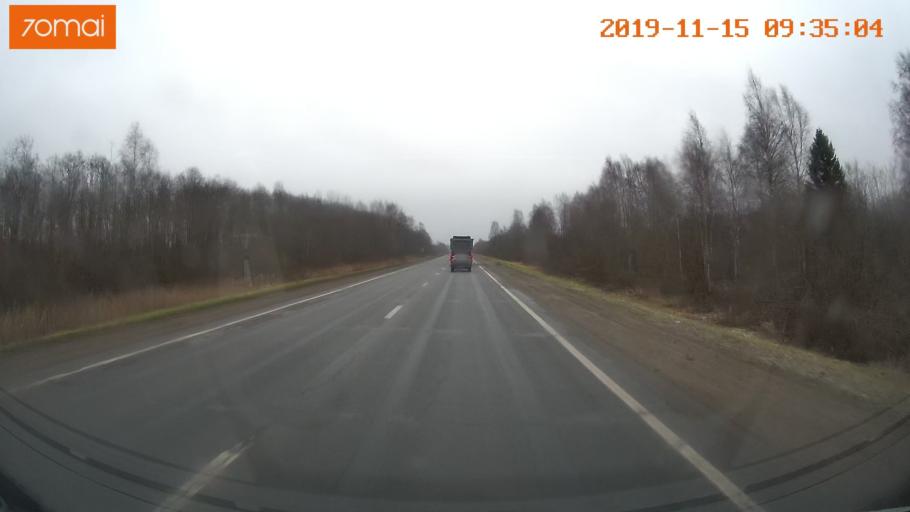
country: RU
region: Vologda
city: Sheksna
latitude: 59.2564
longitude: 38.3921
